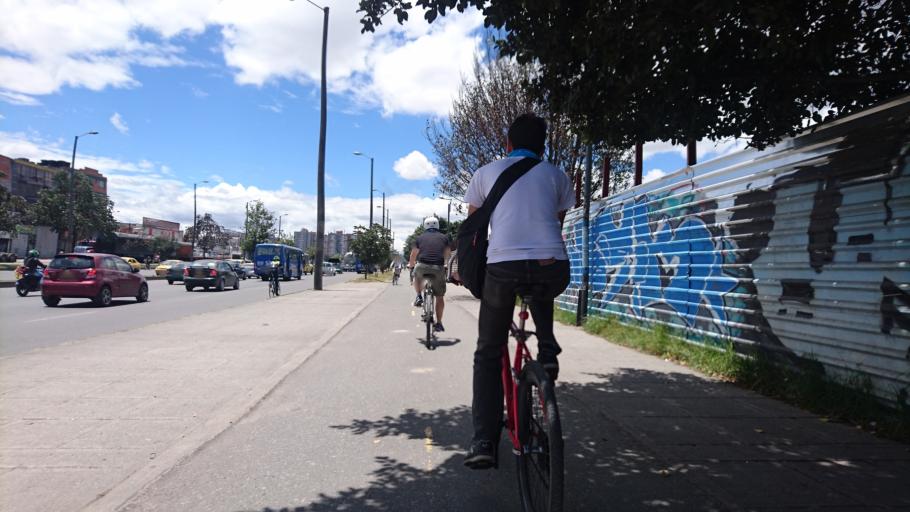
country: CO
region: Bogota D.C.
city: Bogota
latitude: 4.6470
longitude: -74.1494
